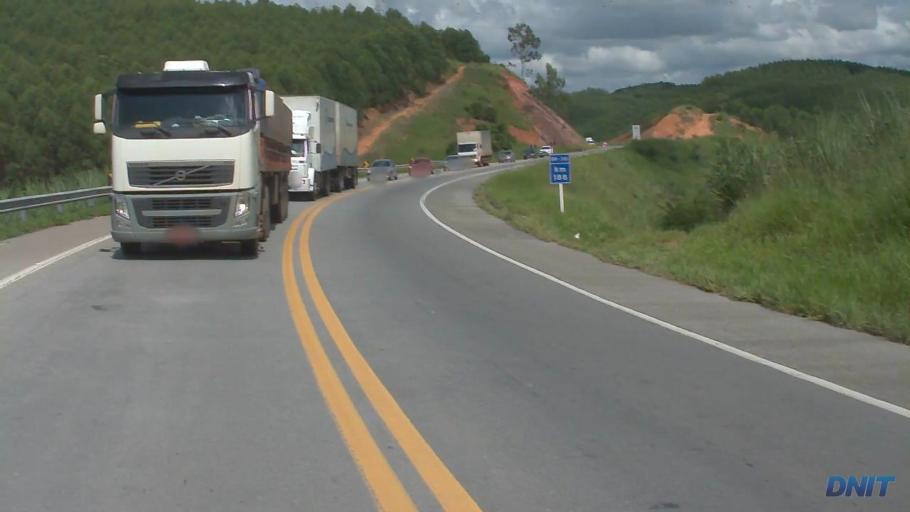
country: BR
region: Minas Gerais
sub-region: Governador Valadares
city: Governador Valadares
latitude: -19.0685
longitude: -42.1740
